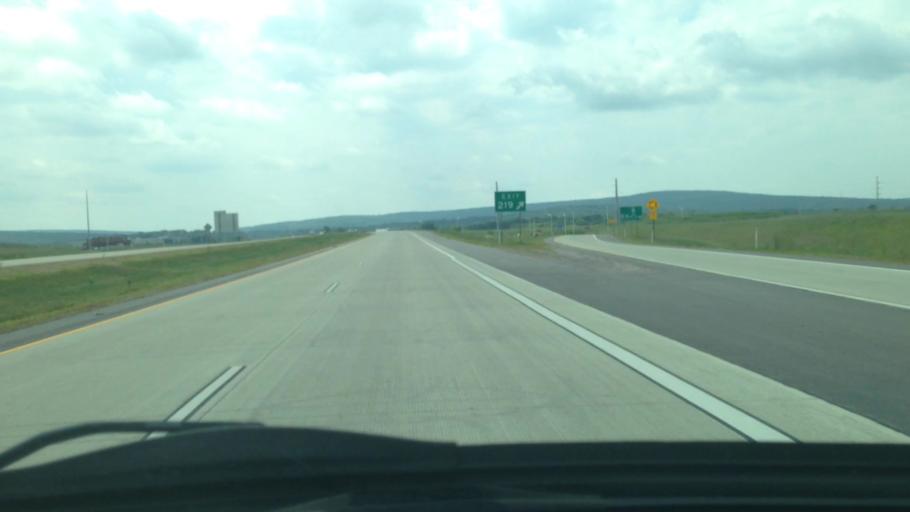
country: US
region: Wisconsin
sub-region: Sauk County
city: West Baraboo
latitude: 43.4640
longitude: -89.7776
